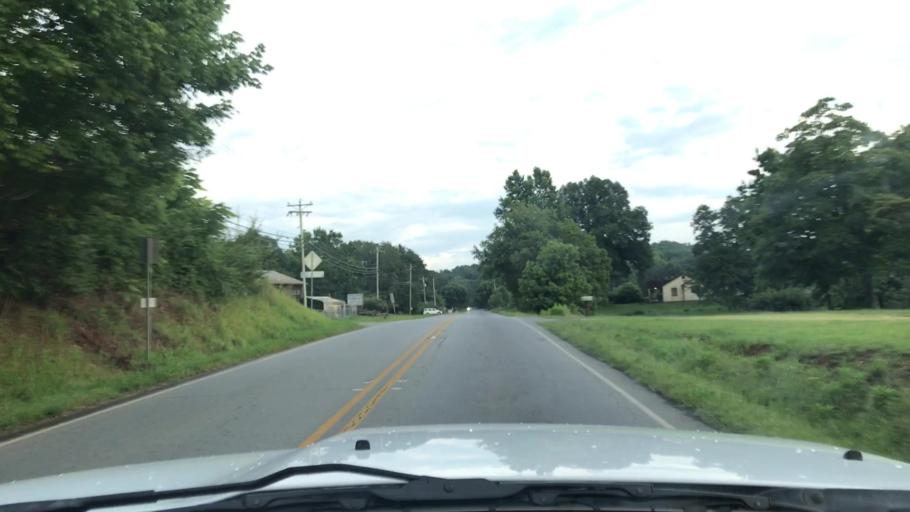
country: US
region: Georgia
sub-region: Fannin County
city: Blue Ridge
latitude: 34.9023
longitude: -84.2660
